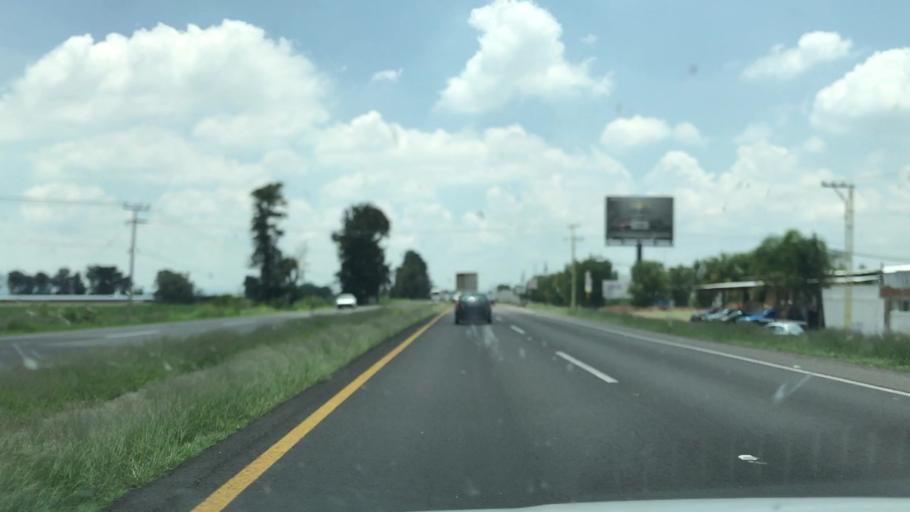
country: MX
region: Guanajuato
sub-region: Irapuato
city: San Jose de Bernalejo (El Guayabo)
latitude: 20.6147
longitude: -101.4049
